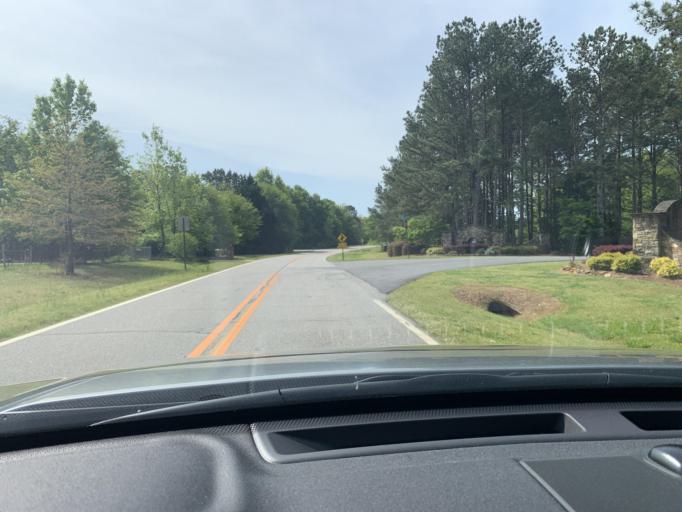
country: US
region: Georgia
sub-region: Oconee County
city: Watkinsville
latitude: 33.8411
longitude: -83.4874
